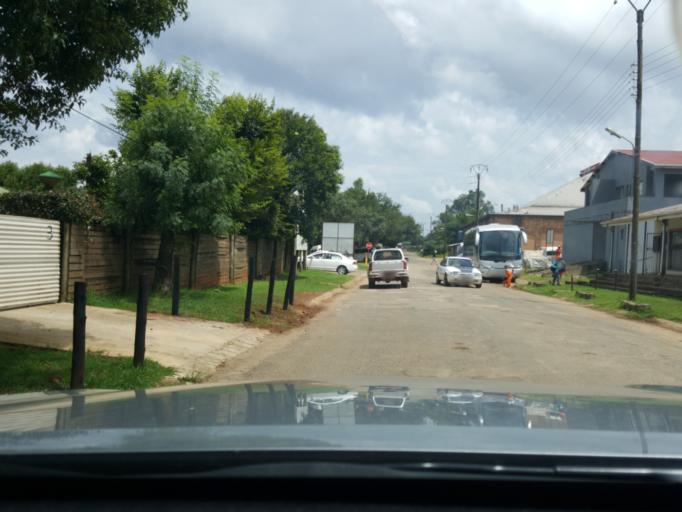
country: ZA
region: Mpumalanga
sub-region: Ehlanzeni District
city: Graksop
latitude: -24.9330
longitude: 30.8418
